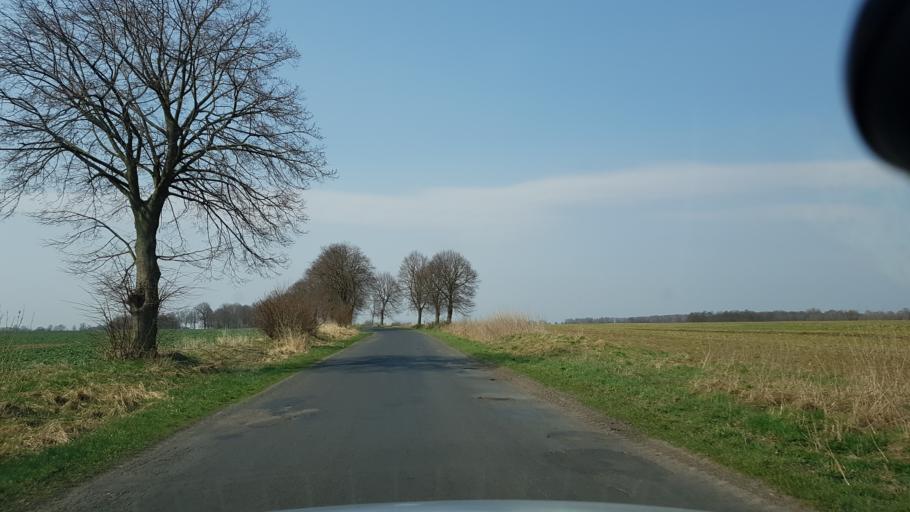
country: PL
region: West Pomeranian Voivodeship
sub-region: Powiat stargardzki
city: Stara Dabrowa
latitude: 53.3570
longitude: 15.1309
